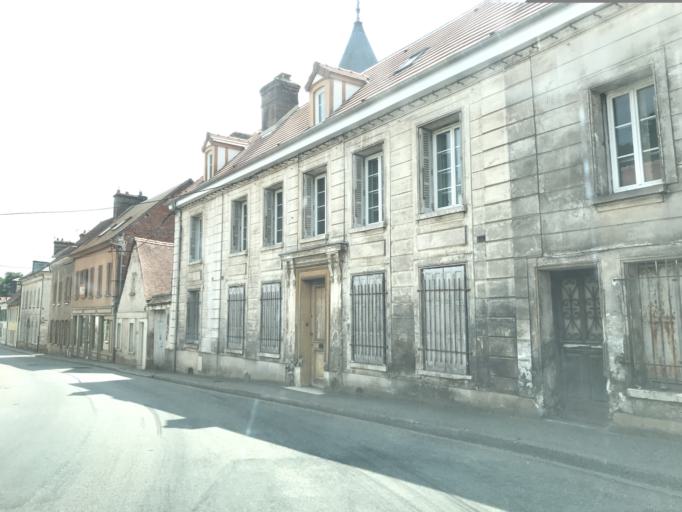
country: FR
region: Haute-Normandie
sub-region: Departement de l'Eure
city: Breuilpont
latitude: 48.9632
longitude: 1.4260
